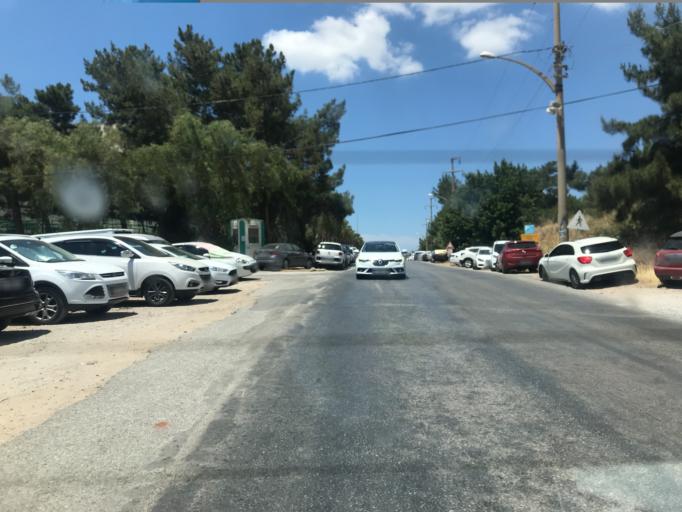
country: TR
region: Aydin
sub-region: Didim
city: Didim
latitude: 37.4125
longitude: 27.3957
